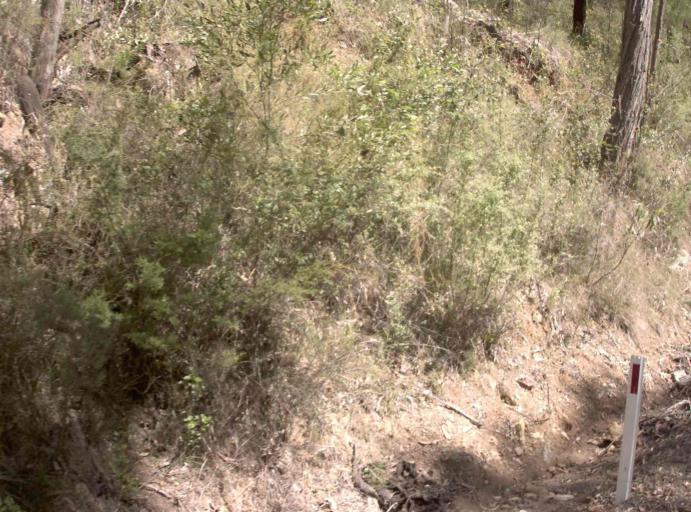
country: AU
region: Victoria
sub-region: East Gippsland
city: Lakes Entrance
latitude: -37.3680
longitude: 148.2186
